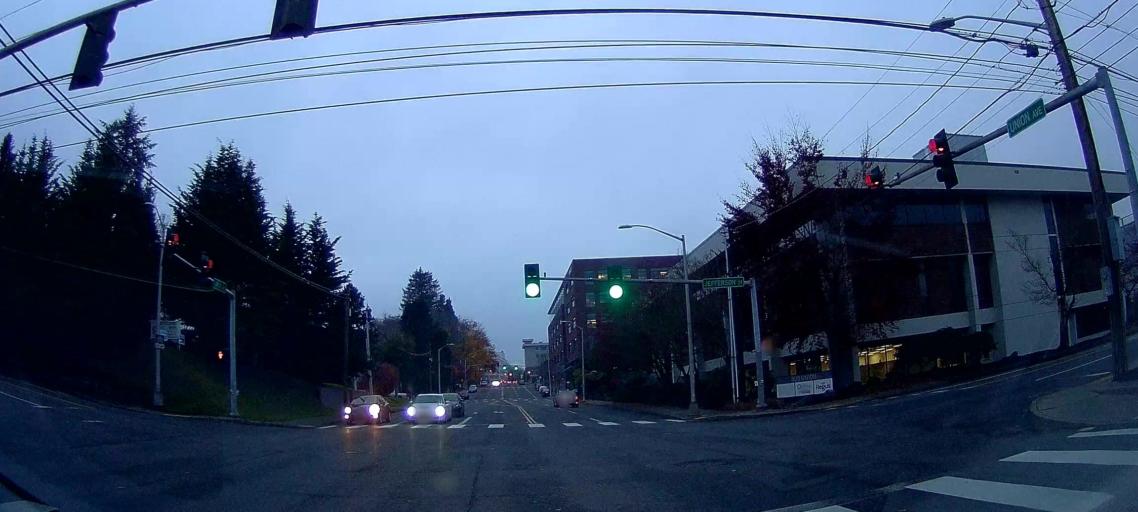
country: US
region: Washington
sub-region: Thurston County
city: Olympia
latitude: 47.0393
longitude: -122.8956
